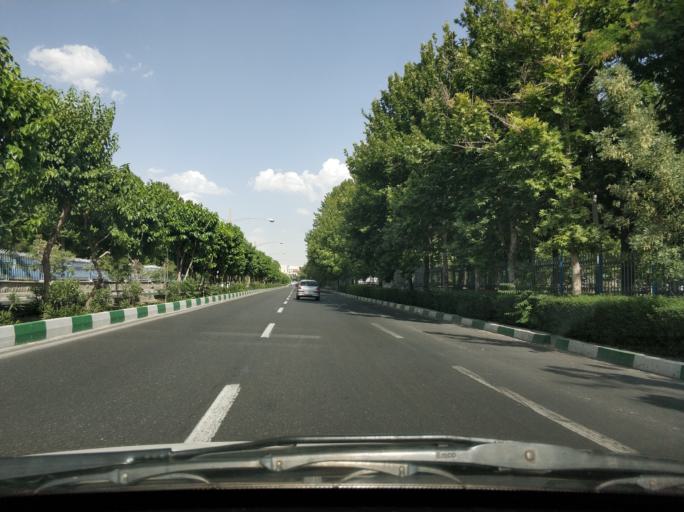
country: IR
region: Tehran
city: Tajrish
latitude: 35.7436
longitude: 51.5808
